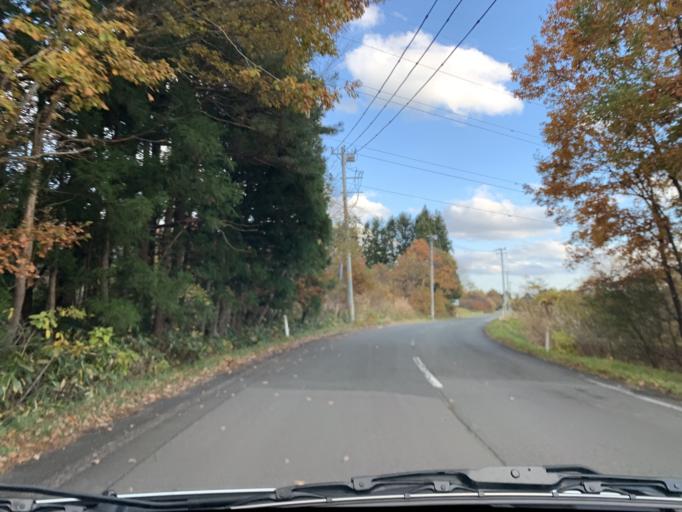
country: JP
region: Iwate
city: Mizusawa
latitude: 39.0966
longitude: 141.0072
